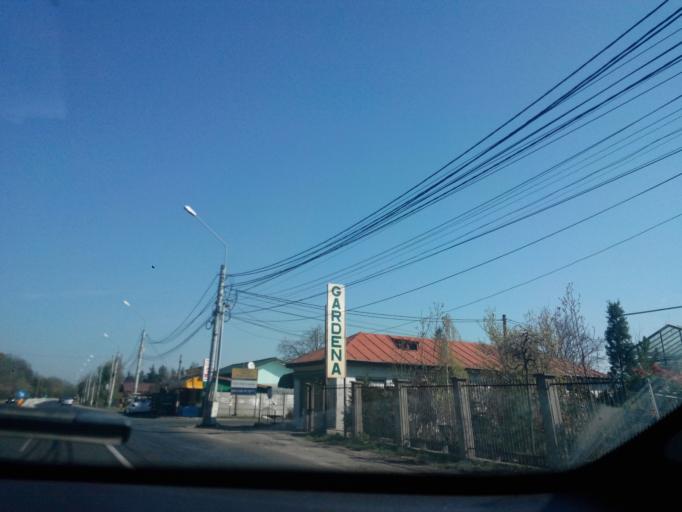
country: RO
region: Ilfov
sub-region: Comuna Corbeanca
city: Corbeanca
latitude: 44.6390
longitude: 26.0687
